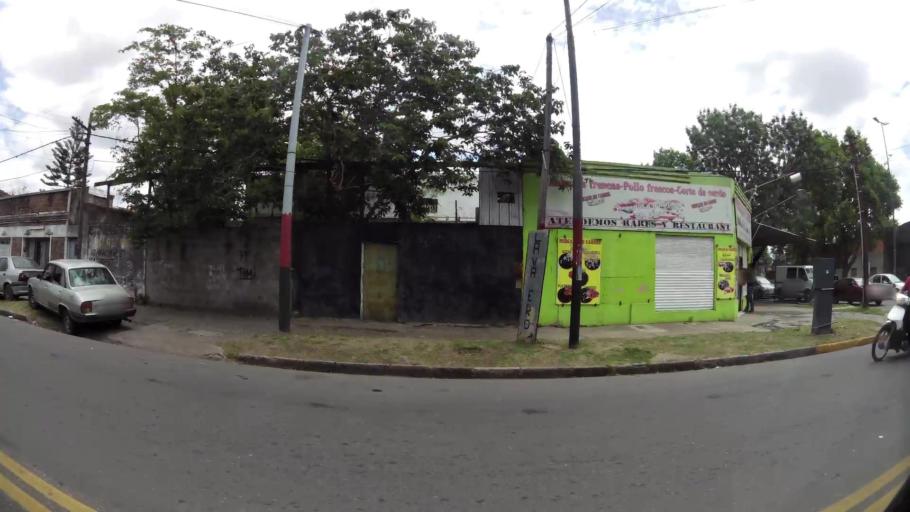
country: AR
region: Santa Fe
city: Gobernador Galvez
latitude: -32.9906
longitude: -60.6369
